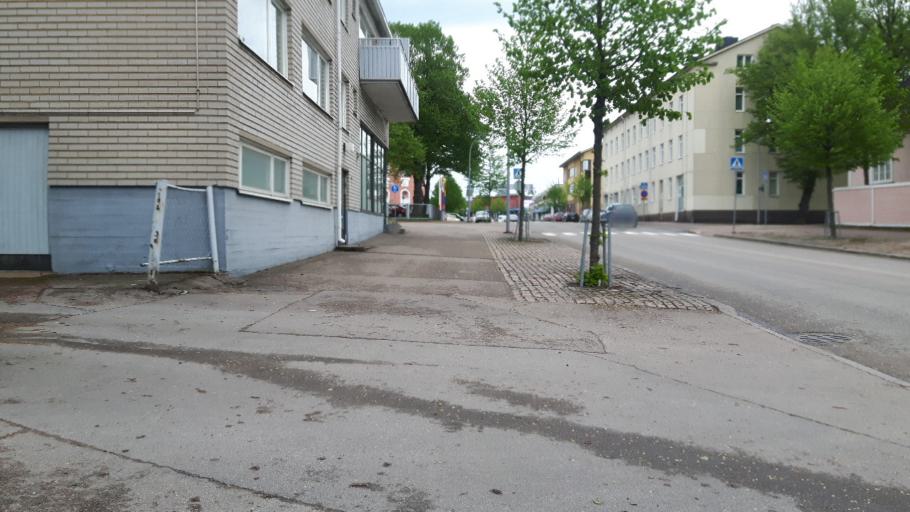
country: FI
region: Kymenlaakso
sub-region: Kotka-Hamina
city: Hamina
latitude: 60.5666
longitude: 27.1912
